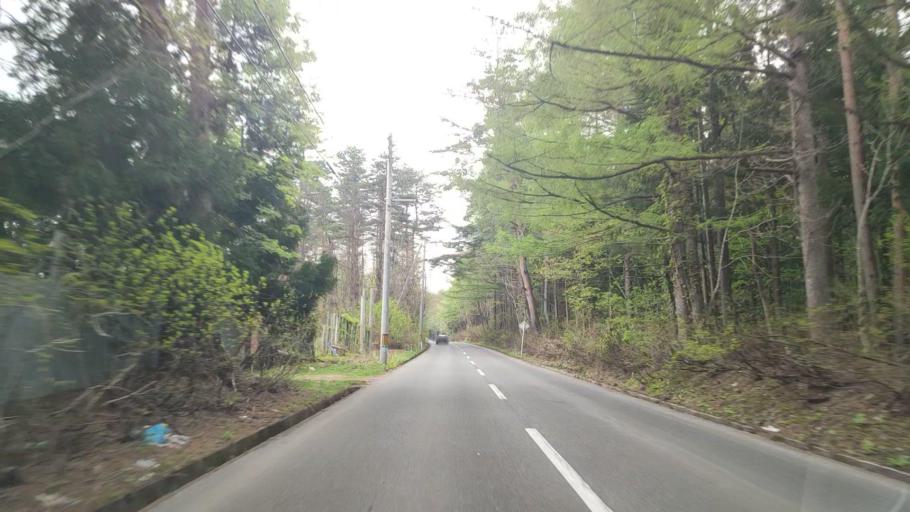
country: JP
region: Aomori
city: Aomori Shi
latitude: 40.7467
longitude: 140.8219
